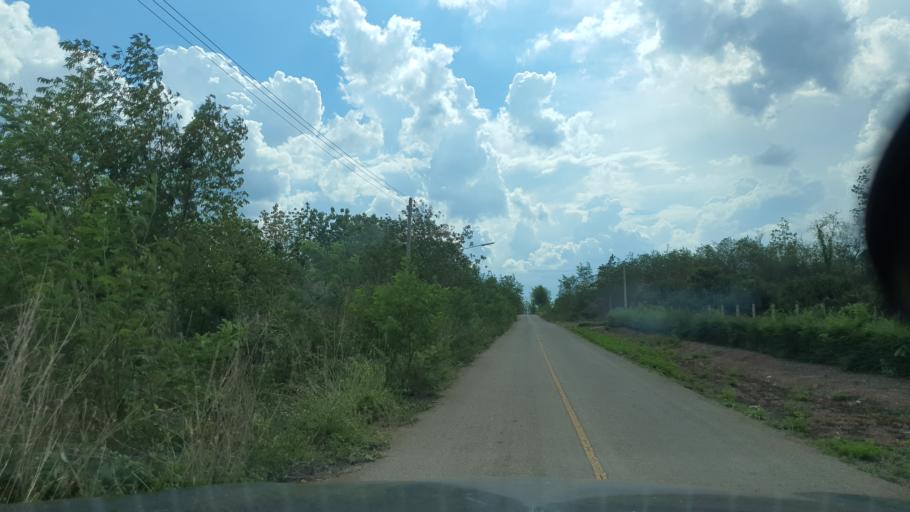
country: TH
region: Chiang Mai
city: Mae Taeng
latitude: 19.1309
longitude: 99.0451
